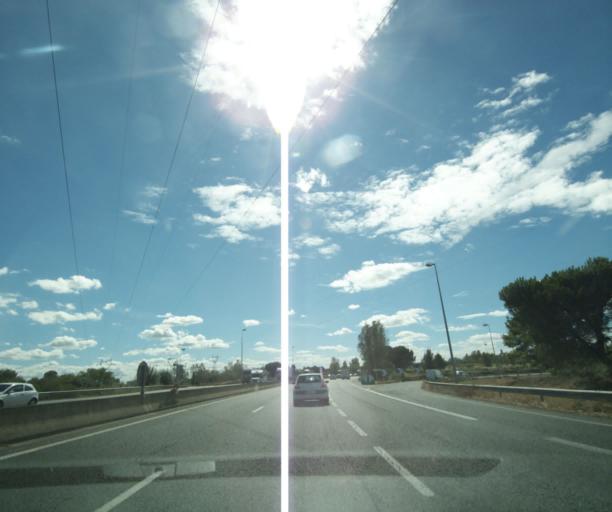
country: FR
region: Aquitaine
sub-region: Departement de la Gironde
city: Bouliac
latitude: 44.8146
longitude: -0.5208
